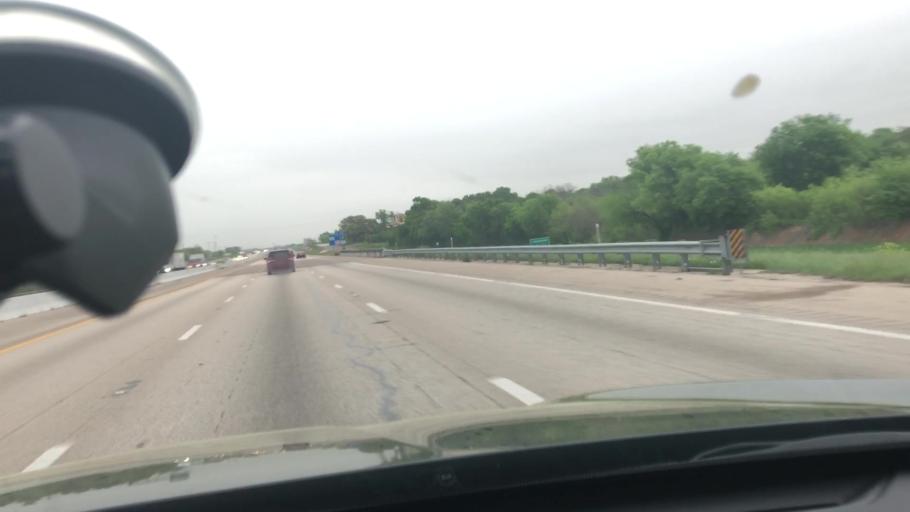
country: US
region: Texas
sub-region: Bell County
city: Belton
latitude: 31.0667
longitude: -97.4285
